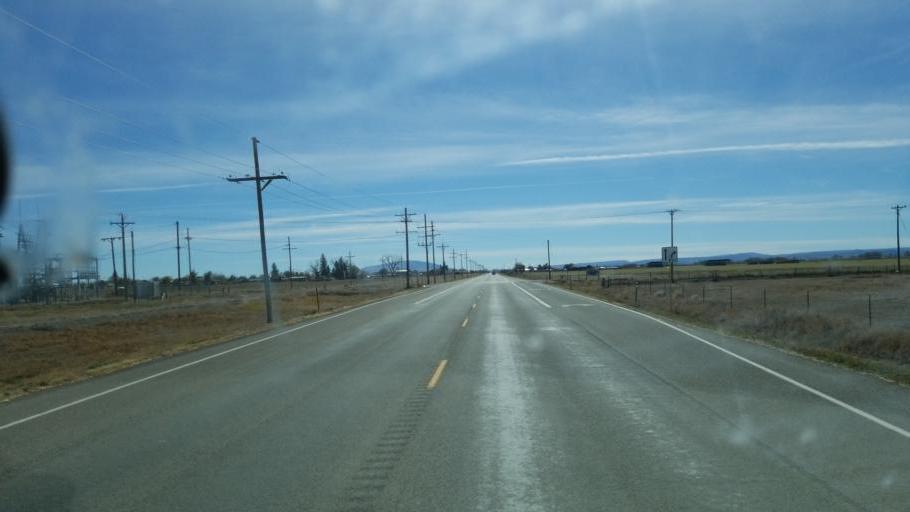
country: US
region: Colorado
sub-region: Conejos County
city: Conejos
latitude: 37.1825
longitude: -105.9856
